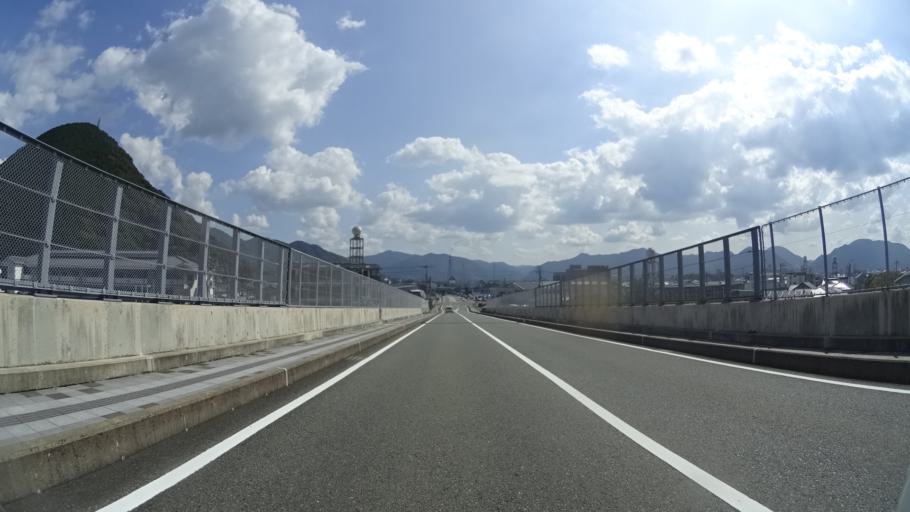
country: JP
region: Yamaguchi
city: Hagi
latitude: 34.4234
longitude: 131.4126
